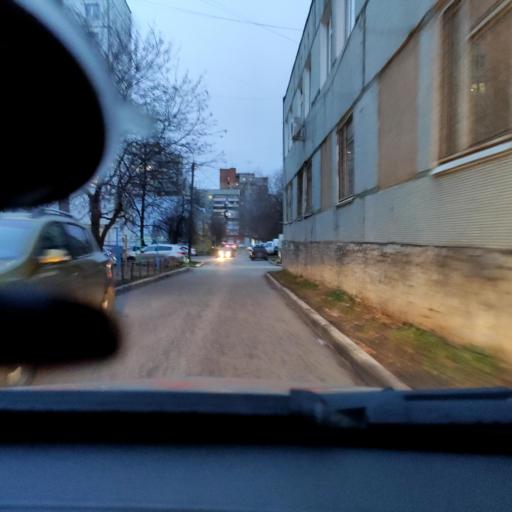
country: RU
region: Bashkortostan
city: Ufa
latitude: 54.7169
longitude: 56.0122
